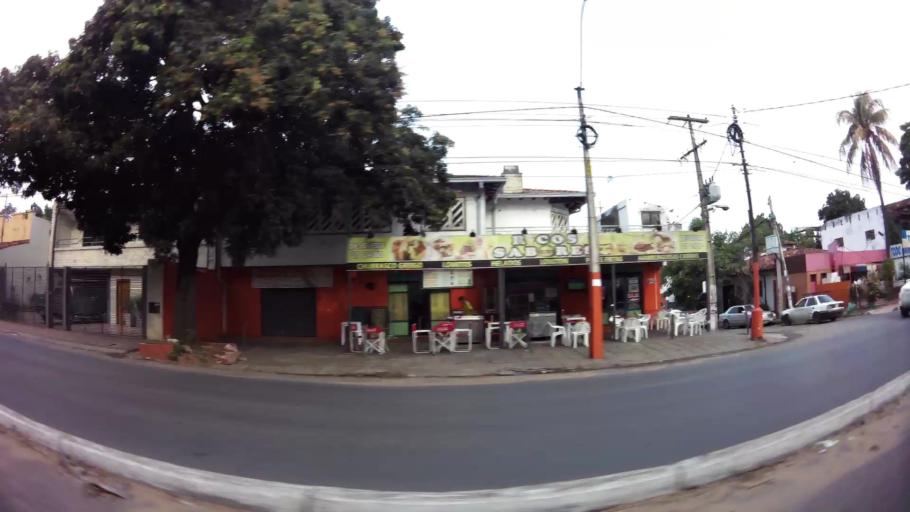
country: PY
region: Asuncion
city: Asuncion
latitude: -25.3060
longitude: -57.6148
